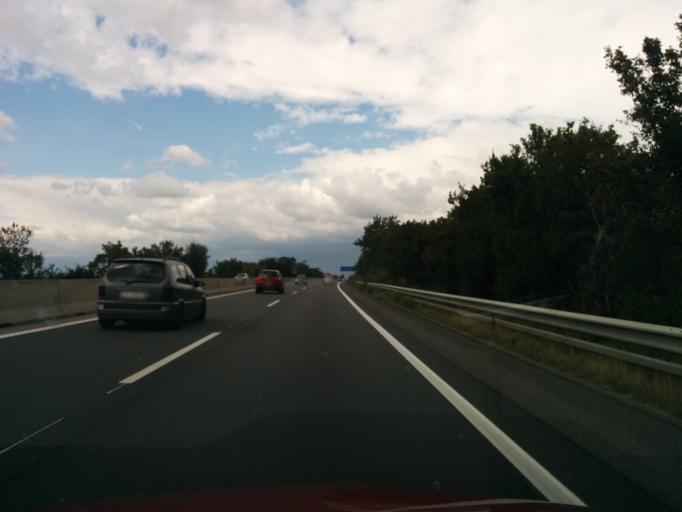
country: AT
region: Lower Austria
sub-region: Politischer Bezirk Wien-Umgebung
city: Fischamend Dorf
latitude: 48.1031
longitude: 16.6464
